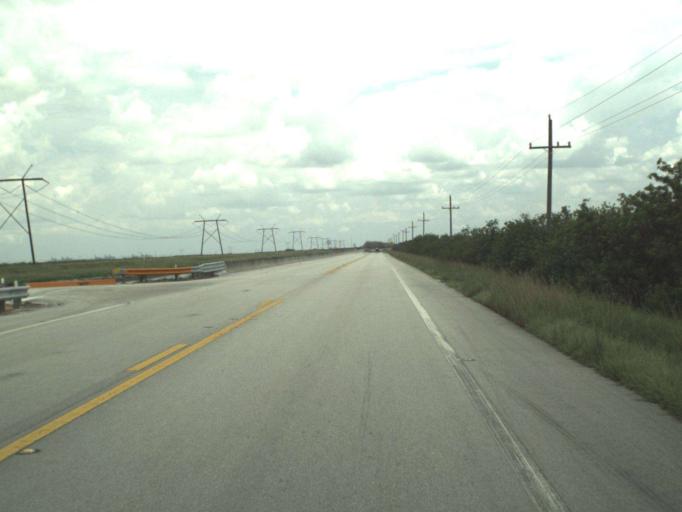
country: US
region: Florida
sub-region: Palm Beach County
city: Loxahatchee Groves
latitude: 26.7331
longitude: -80.4579
